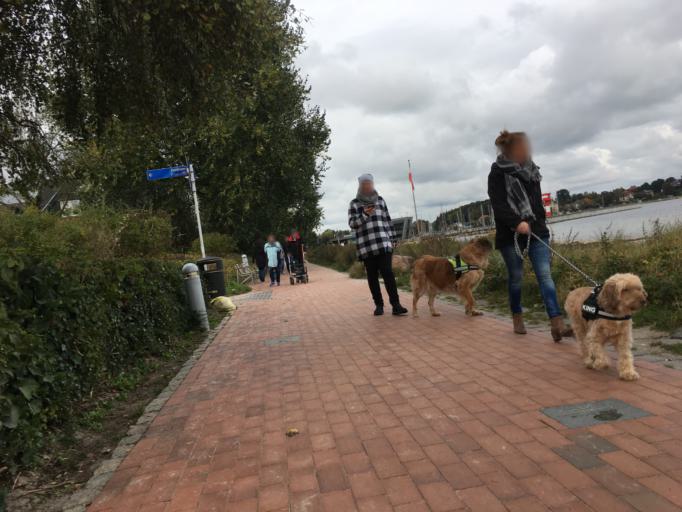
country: DE
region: Schleswig-Holstein
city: Eckernforde
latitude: 54.4711
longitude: 9.8403
